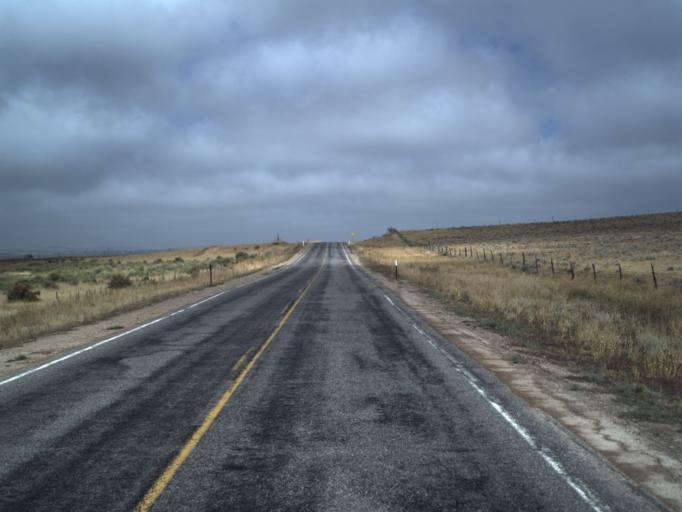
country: US
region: Utah
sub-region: Rich County
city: Randolph
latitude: 41.4760
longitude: -111.1118
